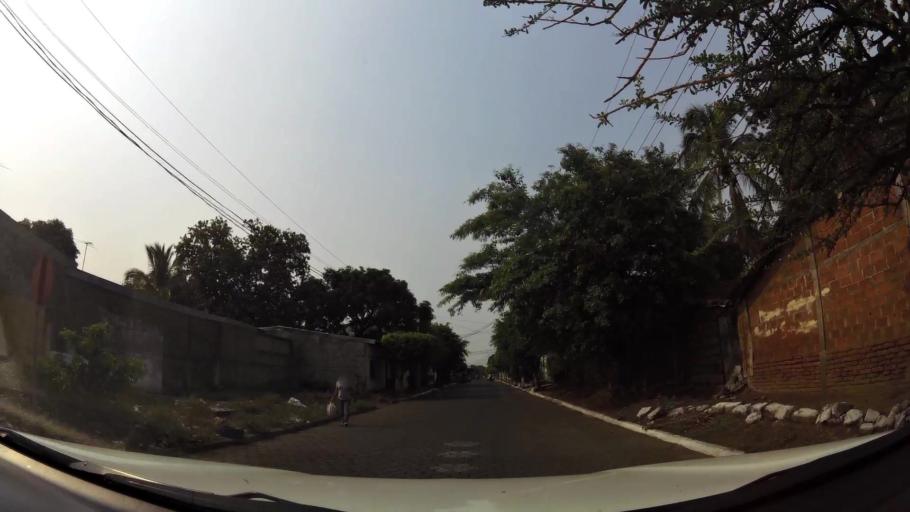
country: NI
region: Chinandega
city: Chinandega
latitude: 12.6313
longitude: -87.1230
